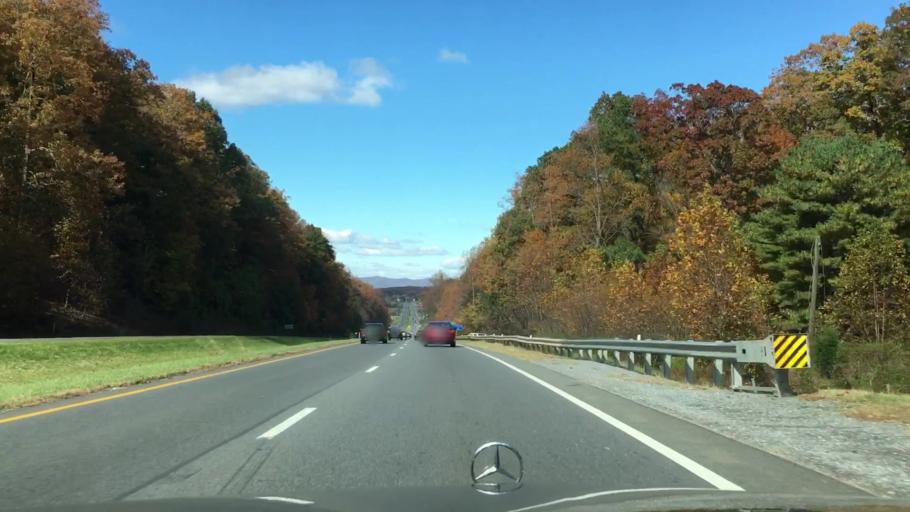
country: US
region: Virginia
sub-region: Campbell County
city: Rustburg
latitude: 37.2995
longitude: -79.1734
